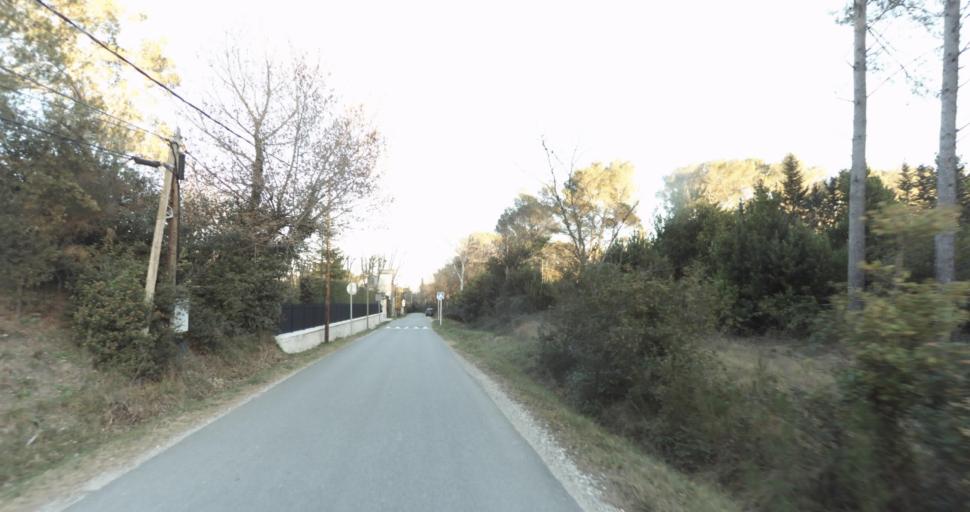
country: FR
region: Provence-Alpes-Cote d'Azur
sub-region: Departement des Bouches-du-Rhone
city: Barbentane
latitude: 43.8844
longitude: 4.7513
